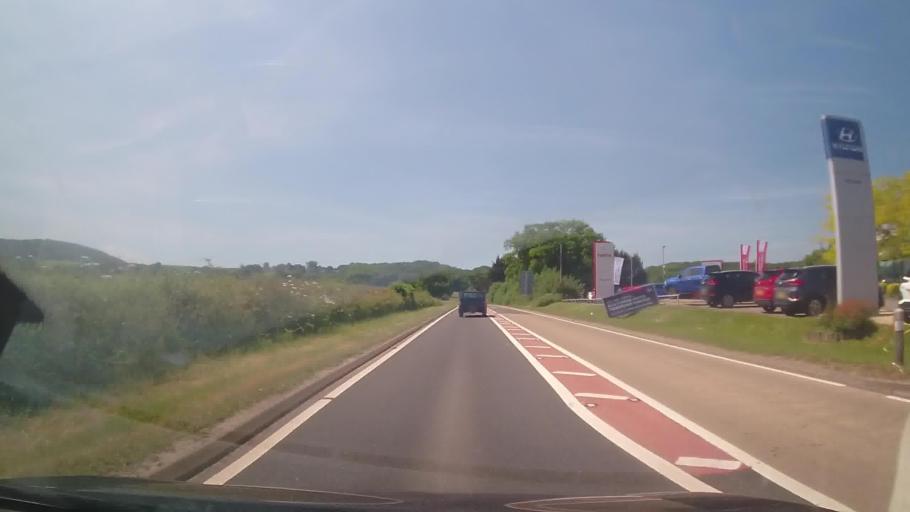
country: GB
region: England
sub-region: Herefordshire
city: Callow
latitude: 52.0149
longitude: -2.7331
